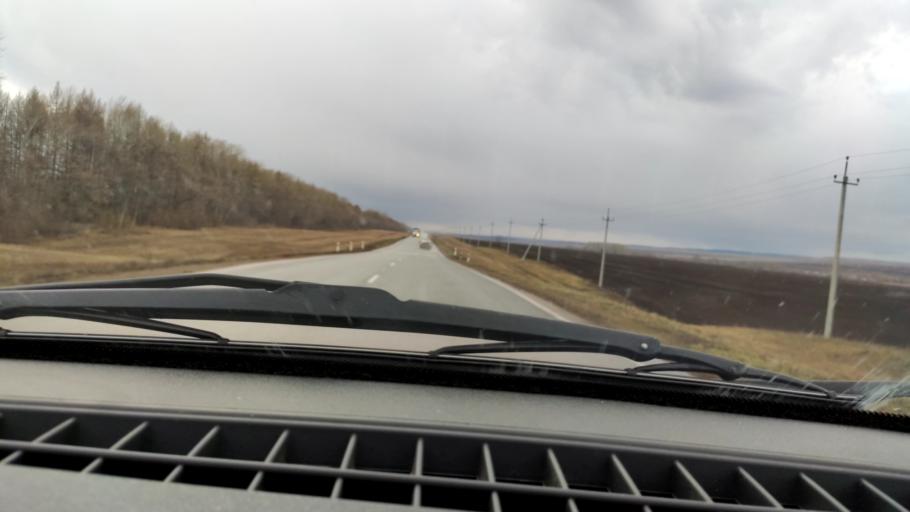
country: RU
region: Bashkortostan
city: Chekmagush
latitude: 55.1112
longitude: 54.9257
